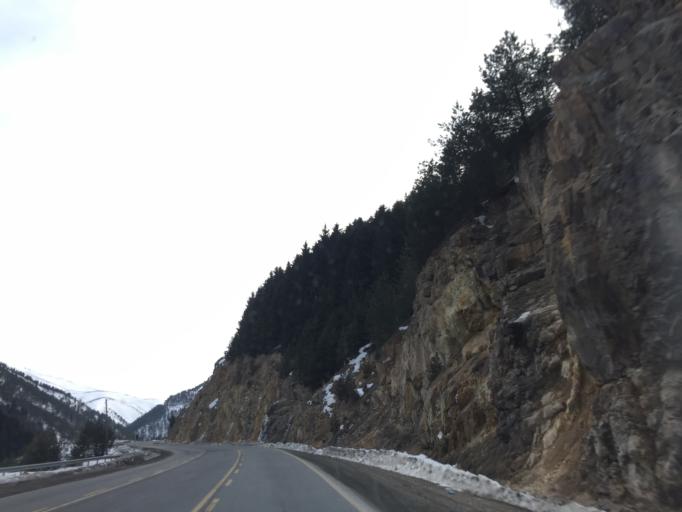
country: TR
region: Gumushane
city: Yaglidere
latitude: 40.6711
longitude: 39.4178
